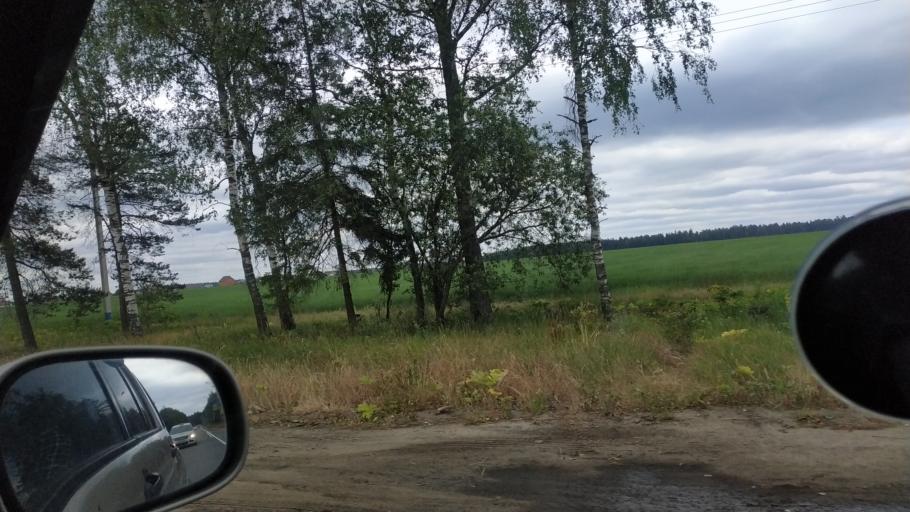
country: RU
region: Moskovskaya
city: Krasnoarmeysk
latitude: 56.0524
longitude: 38.2307
